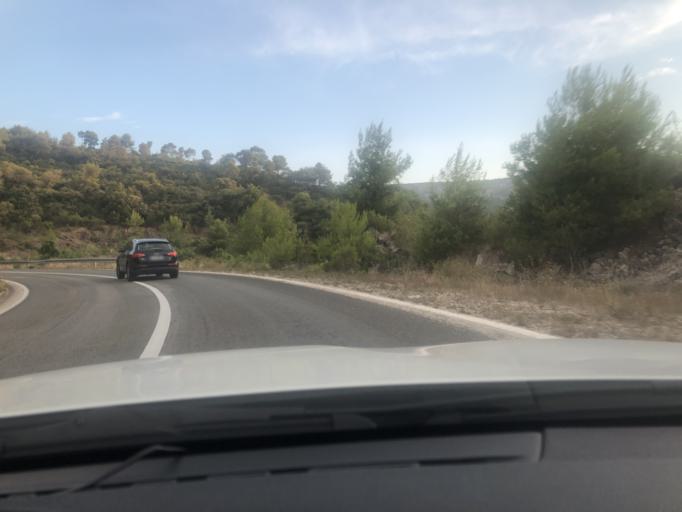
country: HR
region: Splitsko-Dalmatinska
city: Stari Grad
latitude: 43.1728
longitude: 16.5662
